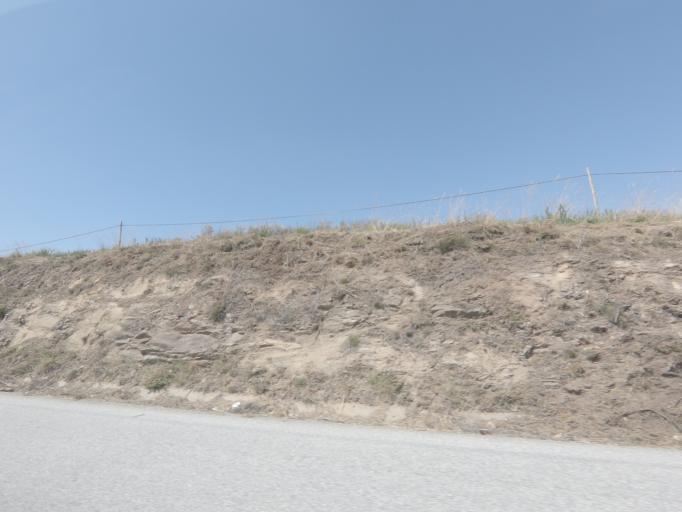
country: PT
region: Viseu
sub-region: Tarouca
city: Tarouca
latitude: 40.9861
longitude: -7.8024
